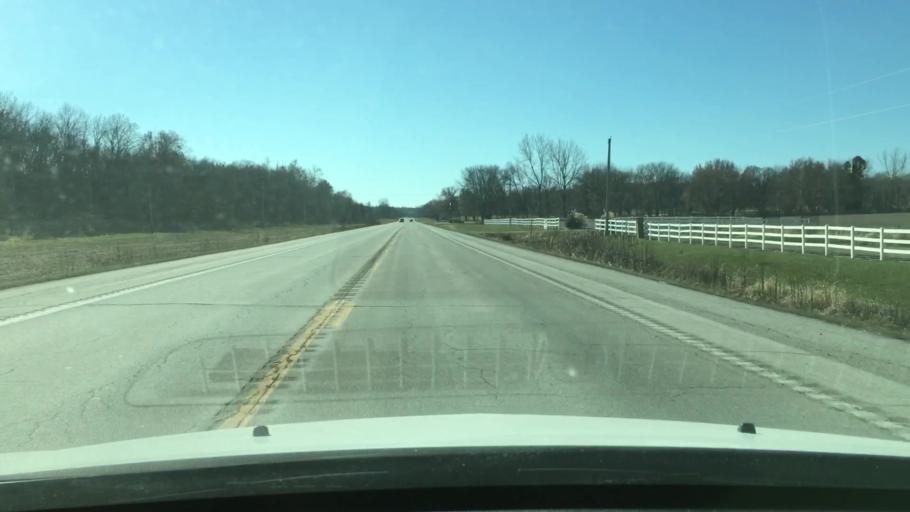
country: US
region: Missouri
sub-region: Pike County
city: Louisiana
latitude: 39.4083
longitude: -91.1043
